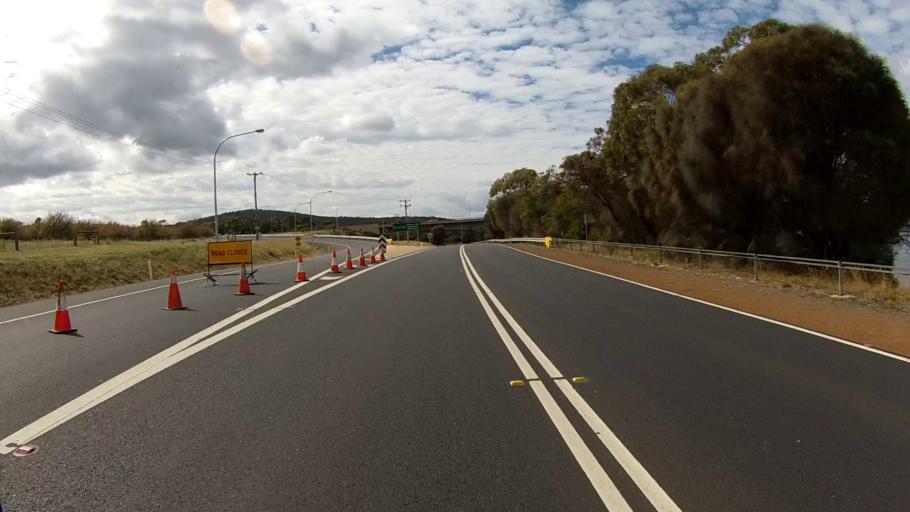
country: AU
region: Tasmania
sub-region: Glenorchy
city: Goodwood
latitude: -42.8126
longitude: 147.3088
